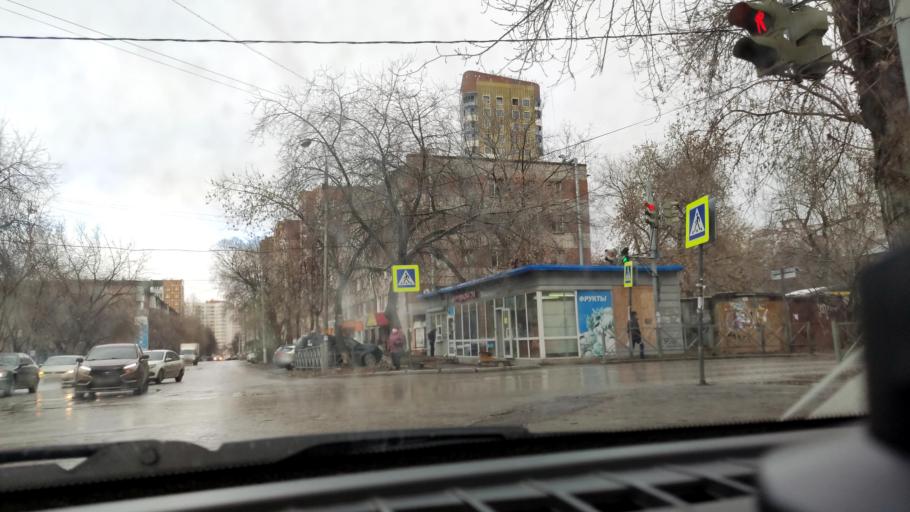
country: RU
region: Perm
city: Perm
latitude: 57.9950
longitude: 56.2420
